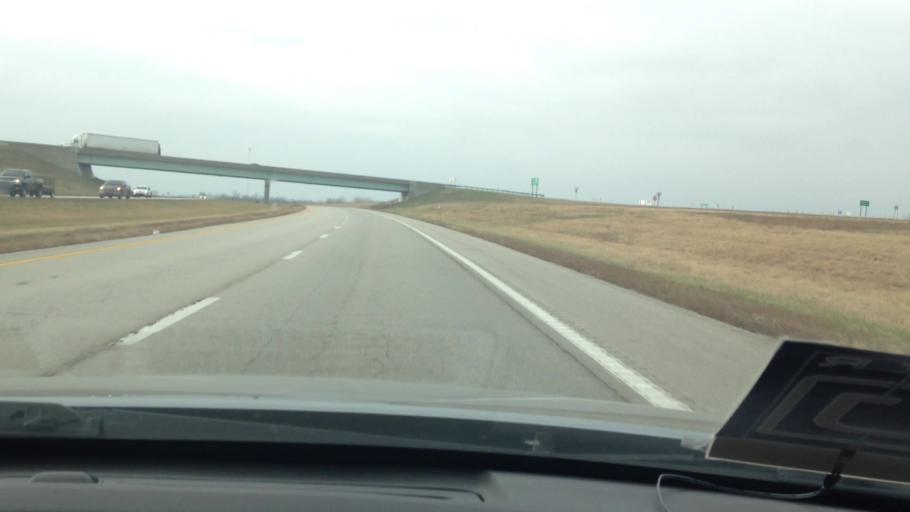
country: US
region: Missouri
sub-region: Cass County
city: Garden City
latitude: 38.5713
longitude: -94.1910
